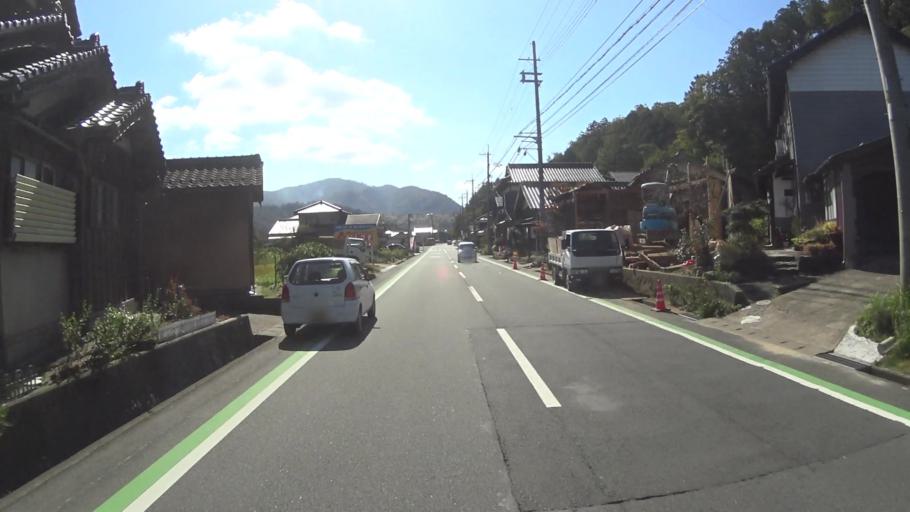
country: JP
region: Kyoto
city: Miyazu
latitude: 35.6564
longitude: 135.0889
